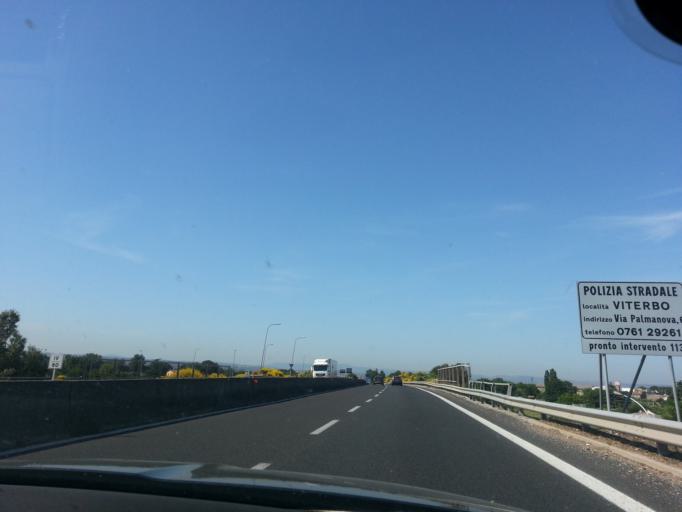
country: IT
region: Latium
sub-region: Provincia di Viterbo
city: Viterbo
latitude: 42.4307
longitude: 12.0837
